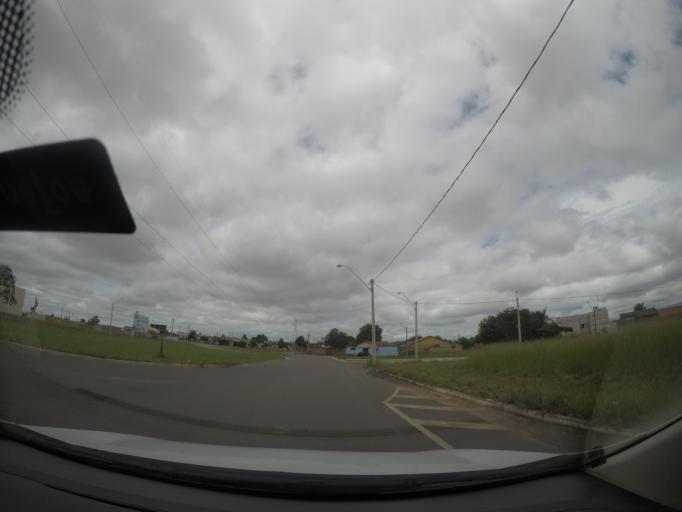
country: BR
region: Goias
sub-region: Goiania
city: Goiania
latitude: -16.7374
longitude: -49.3667
